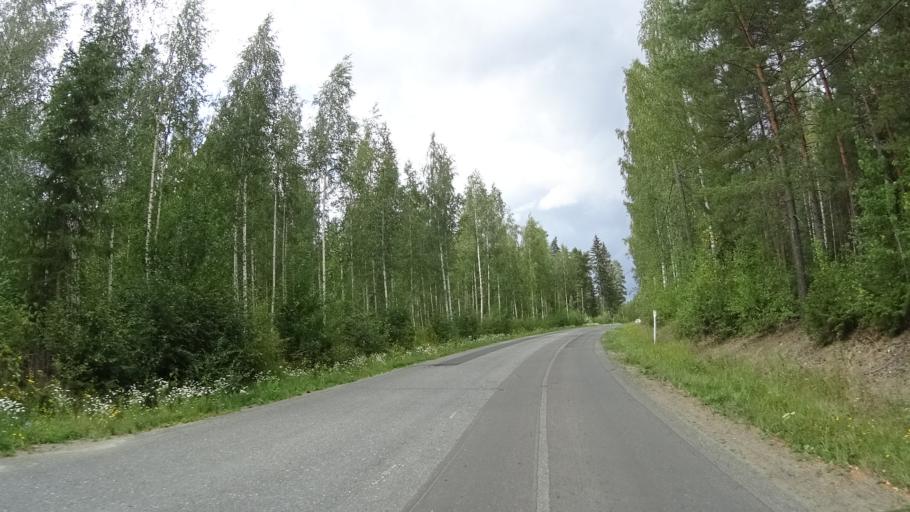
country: FI
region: Pirkanmaa
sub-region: Tampere
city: Kangasala
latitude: 61.4468
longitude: 24.1218
